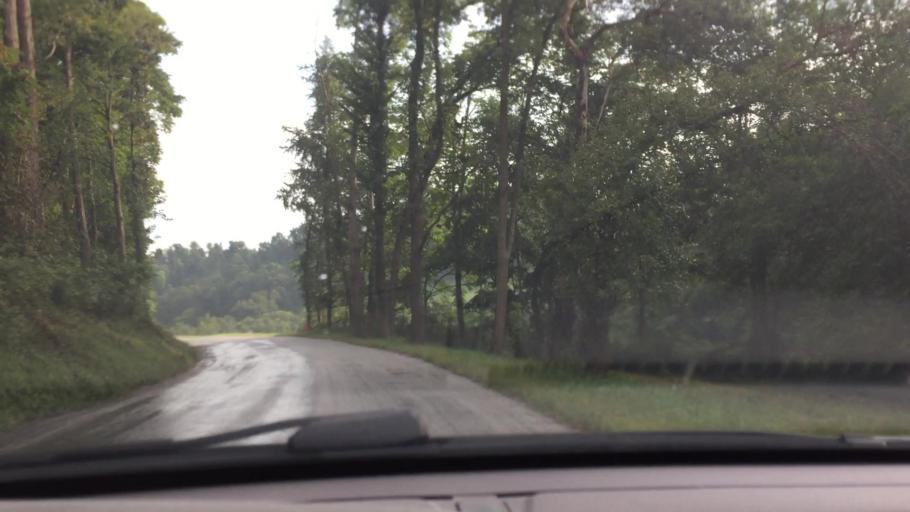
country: US
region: Pennsylvania
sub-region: Washington County
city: McGovern
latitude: 40.2049
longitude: -80.1811
